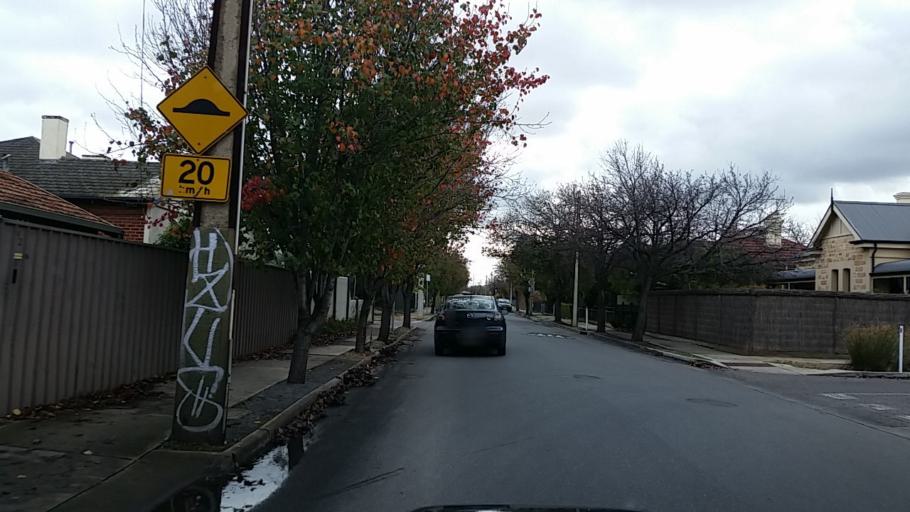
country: AU
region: South Australia
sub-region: City of West Torrens
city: Thebarton
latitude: -34.9281
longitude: 138.5611
